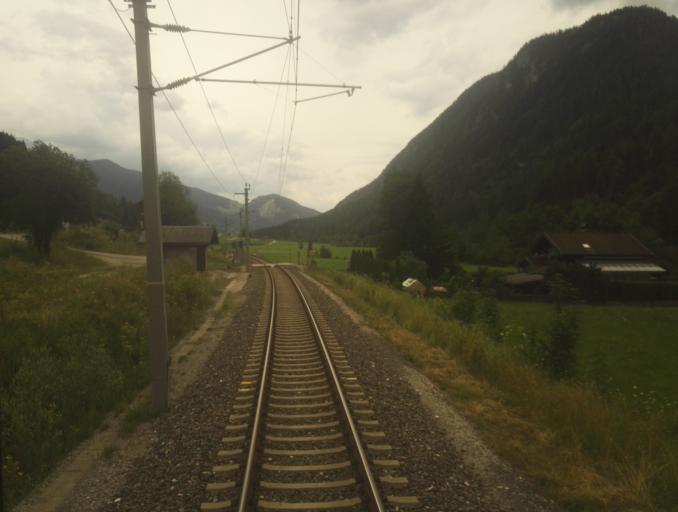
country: AT
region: Salzburg
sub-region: Politischer Bezirk Sankt Johann im Pongau
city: Forstau
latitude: 47.3960
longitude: 13.5244
